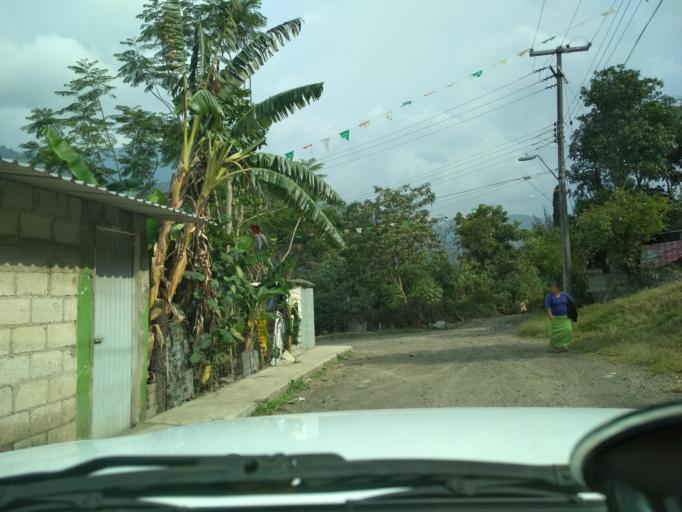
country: MX
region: Veracruz
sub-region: Nogales
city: Agricola Lazaro Cardenas
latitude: 18.7997
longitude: -97.1958
